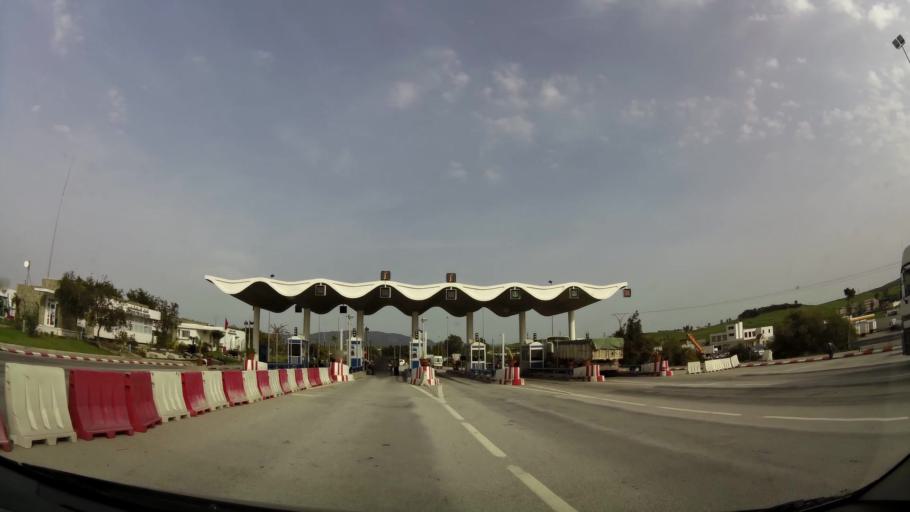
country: MA
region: Tanger-Tetouan
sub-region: Tanger-Assilah
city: Tangier
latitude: 35.6787
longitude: -5.7070
